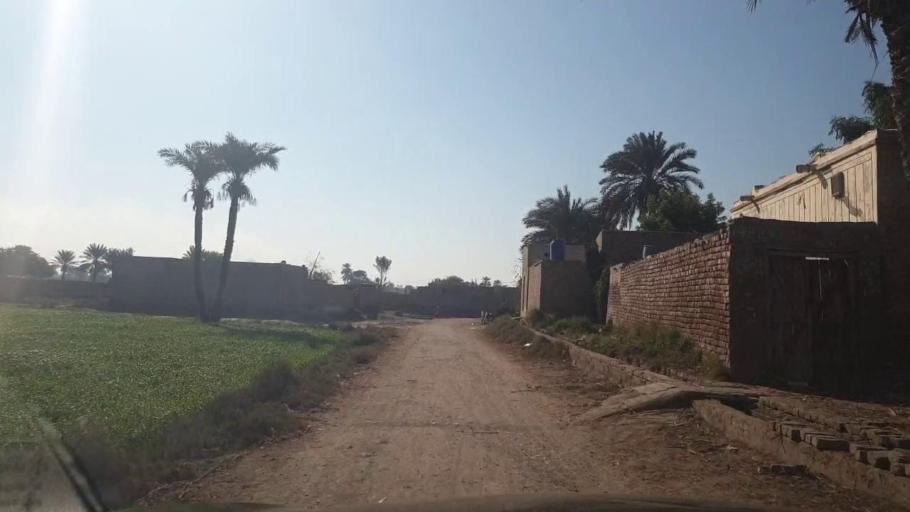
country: PK
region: Sindh
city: Ghotki
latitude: 27.9960
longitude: 69.3271
